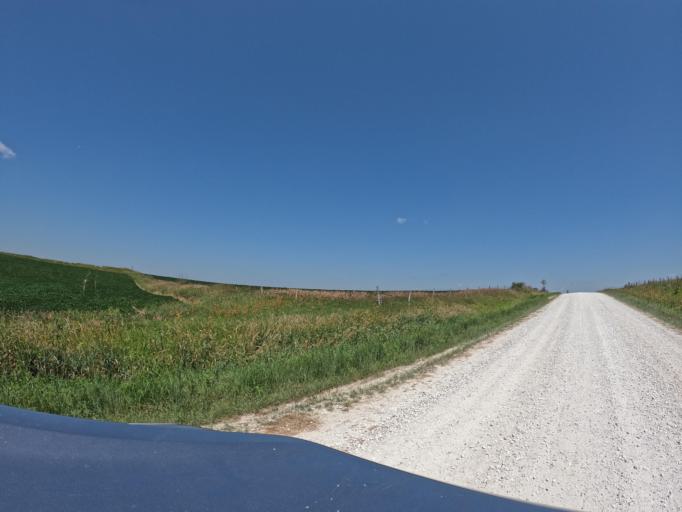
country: US
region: Iowa
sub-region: Keokuk County
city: Sigourney
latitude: 41.2670
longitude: -92.2191
